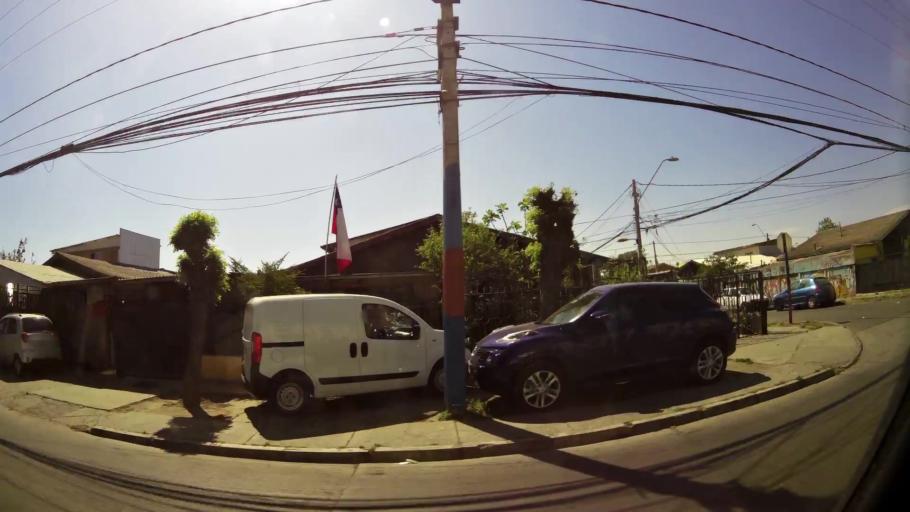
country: CL
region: Santiago Metropolitan
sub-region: Provincia de Santiago
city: Lo Prado
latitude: -33.5160
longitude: -70.7528
